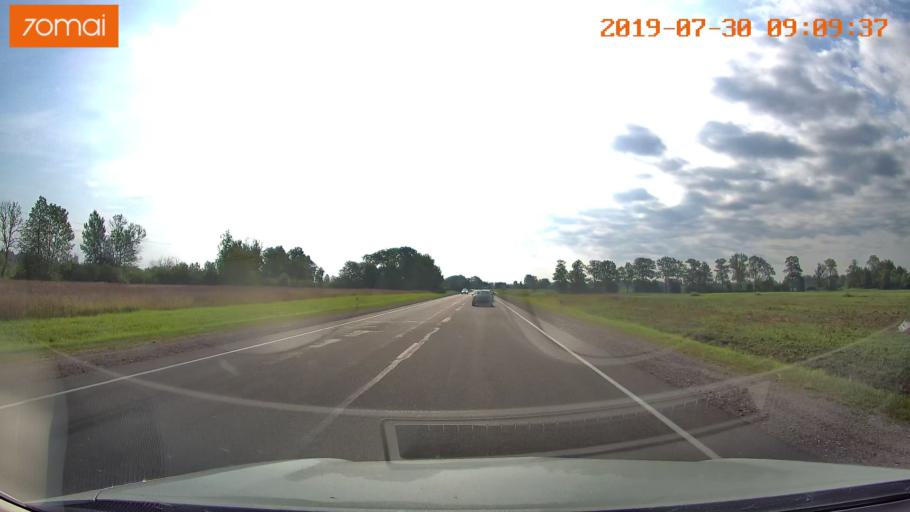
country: RU
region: Kaliningrad
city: Nesterov
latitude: 54.6130
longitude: 22.4117
